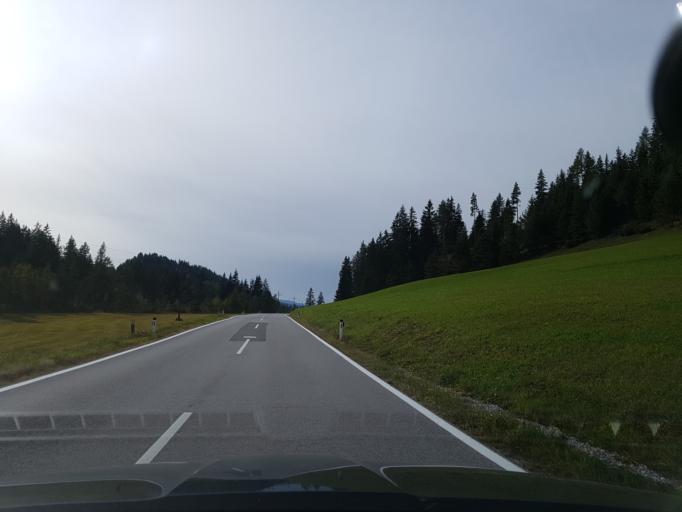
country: AT
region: Salzburg
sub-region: Politischer Bezirk Sankt Johann im Pongau
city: Forstau
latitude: 47.3778
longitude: 13.5182
